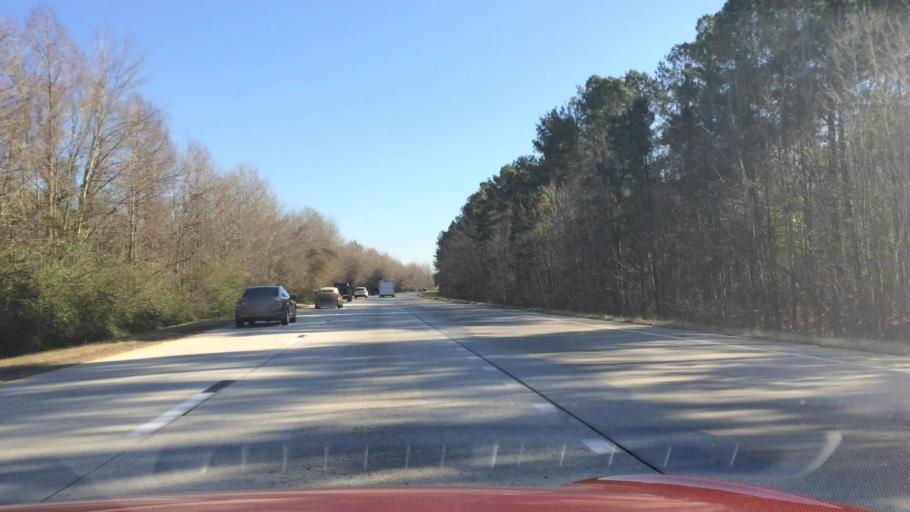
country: US
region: South Carolina
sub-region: Orangeburg County
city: Holly Hill
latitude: 33.2665
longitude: -80.4832
